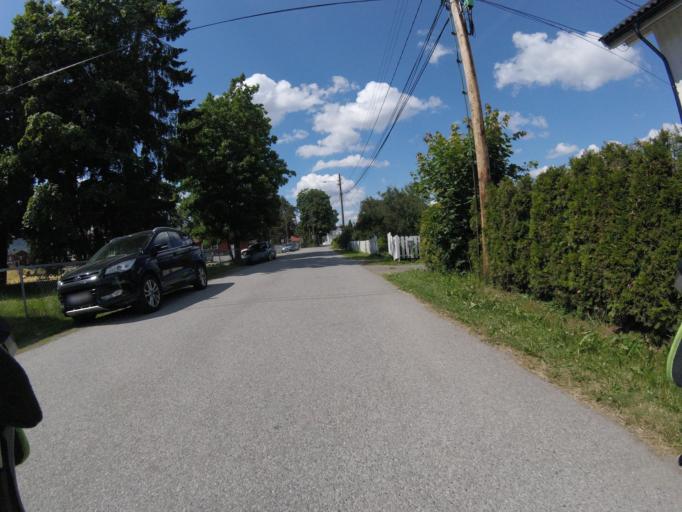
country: NO
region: Akershus
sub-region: Skedsmo
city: Lillestrom
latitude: 59.9544
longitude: 11.0637
